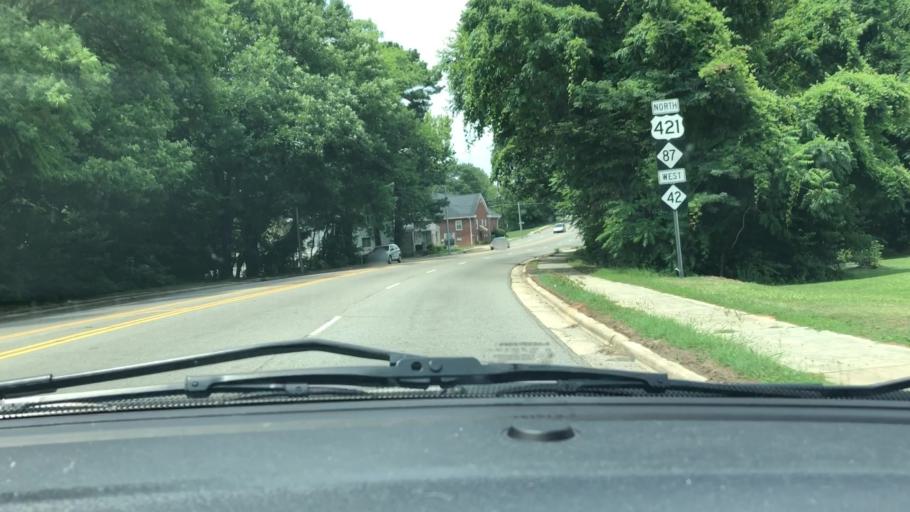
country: US
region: North Carolina
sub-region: Lee County
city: Sanford
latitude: 35.4742
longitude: -79.1779
